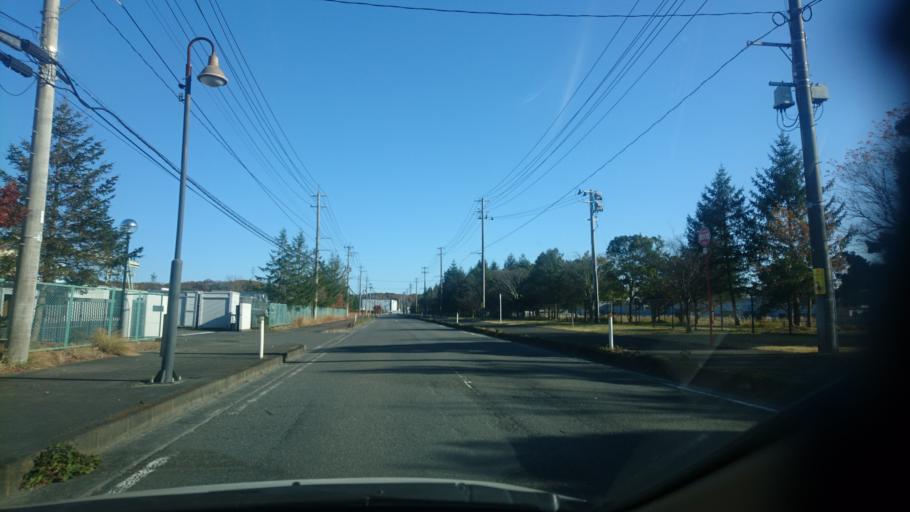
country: JP
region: Miyagi
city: Tomiya
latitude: 38.4645
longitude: 140.9261
